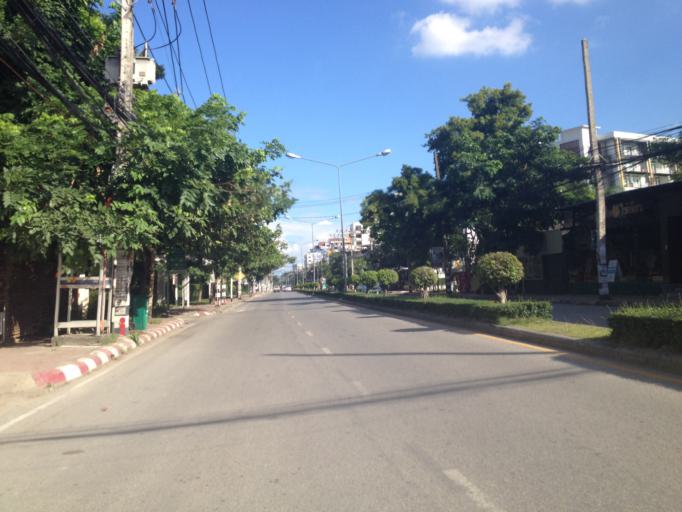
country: TH
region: Chiang Mai
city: Chiang Mai
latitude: 18.8070
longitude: 98.9573
